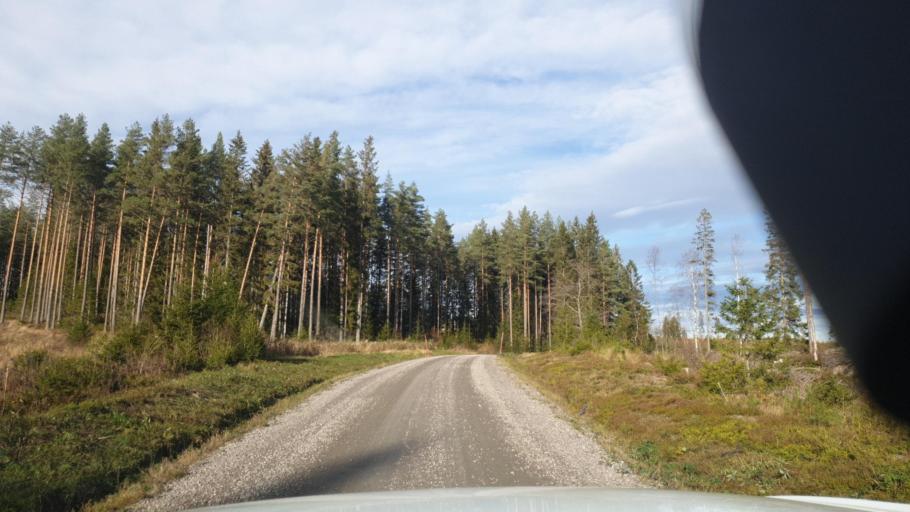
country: SE
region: Vaermland
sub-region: Eda Kommun
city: Charlottenberg
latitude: 60.0600
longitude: 12.5265
